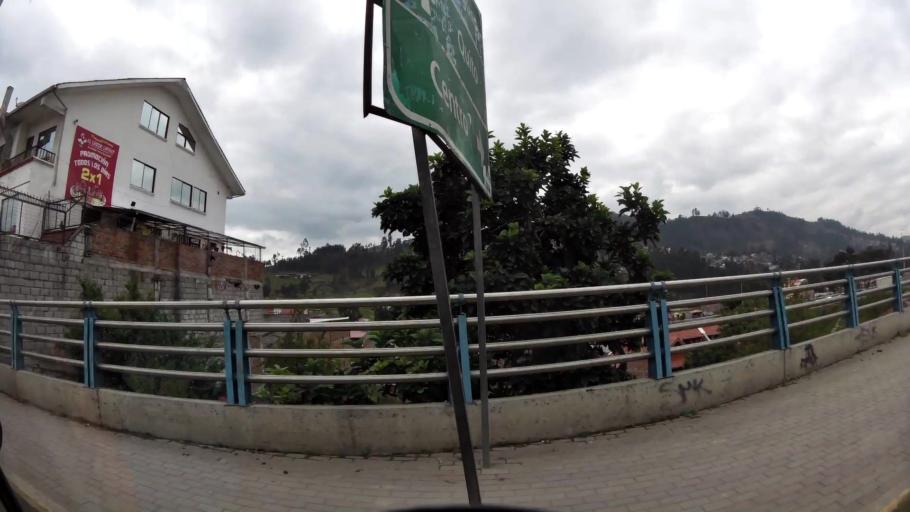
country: EC
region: Azuay
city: Cuenca
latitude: -2.9241
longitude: -79.0398
